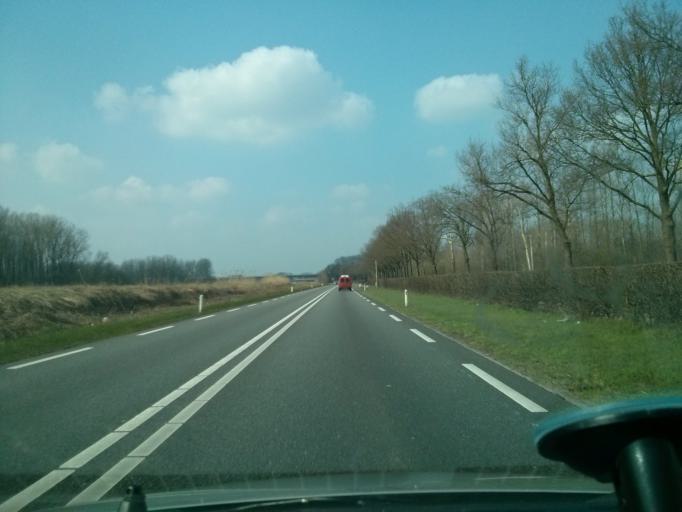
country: NL
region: North Brabant
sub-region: Gemeente Veghel
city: Eerde
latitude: 51.6399
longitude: 5.4741
